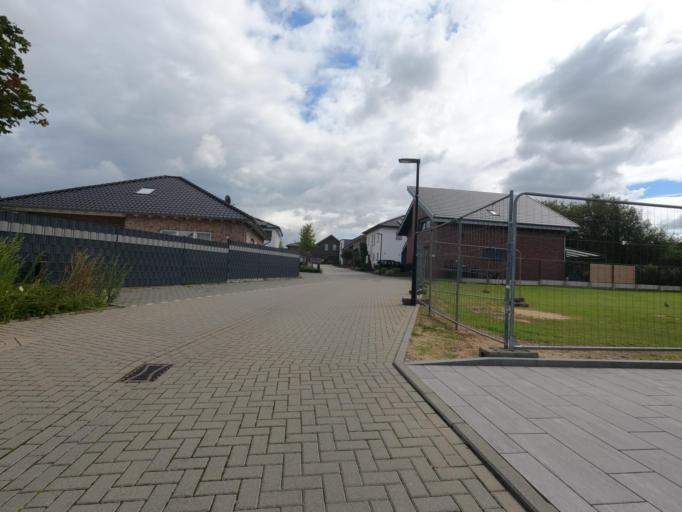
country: DE
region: North Rhine-Westphalia
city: Geilenkirchen
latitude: 50.9640
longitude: 6.1352
